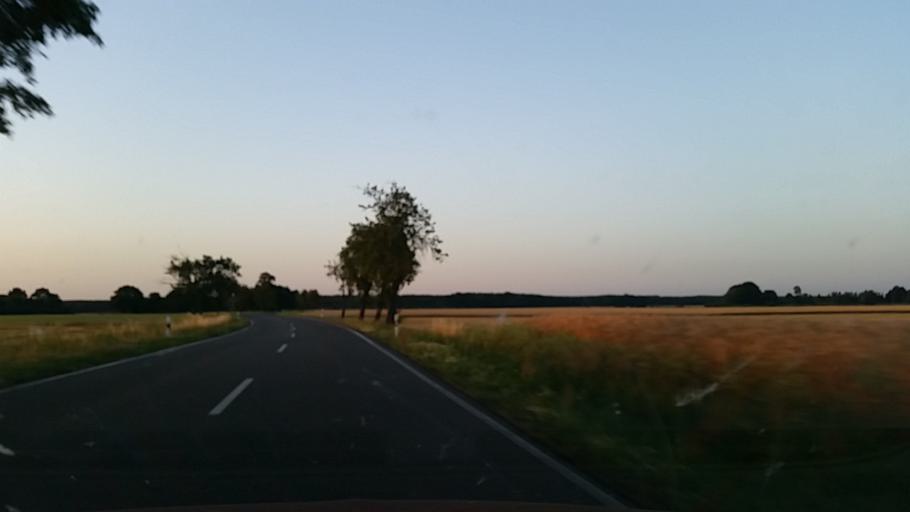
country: DE
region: Saxony-Anhalt
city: Jessen
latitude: 51.7616
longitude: 12.9463
